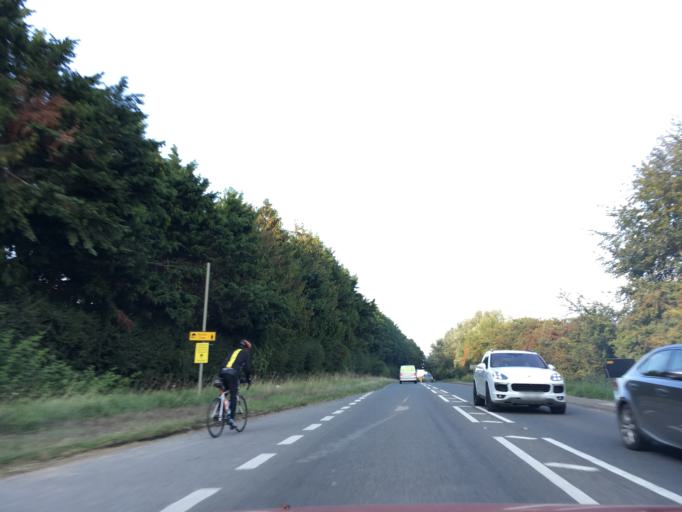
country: GB
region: England
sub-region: Gloucestershire
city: Bourton on the Water
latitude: 51.8879
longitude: -1.7674
